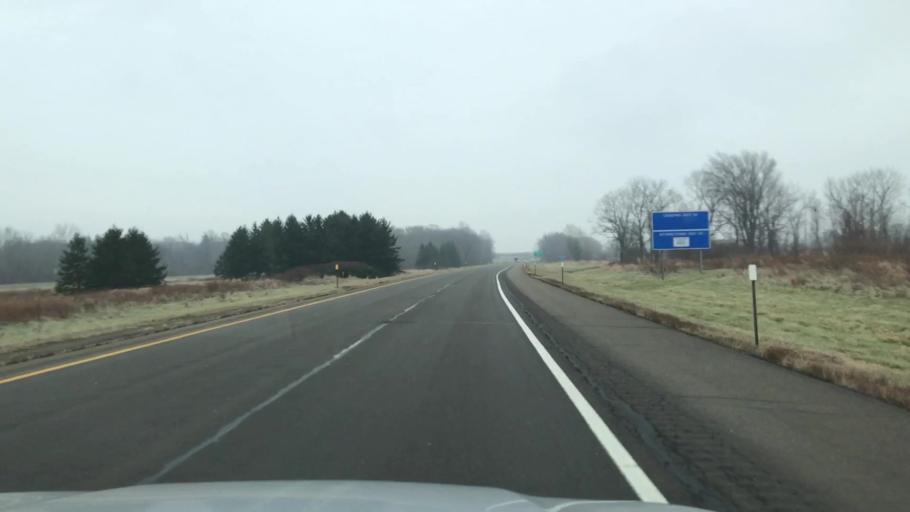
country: US
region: Pennsylvania
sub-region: Erie County
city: North East
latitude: 42.2566
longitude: -79.7553
